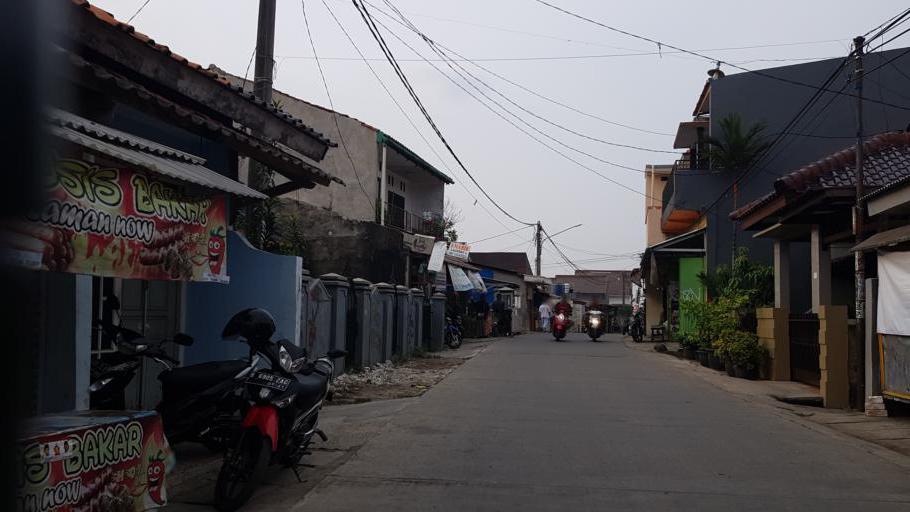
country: ID
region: West Java
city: Depok
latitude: -6.3925
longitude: 106.7977
